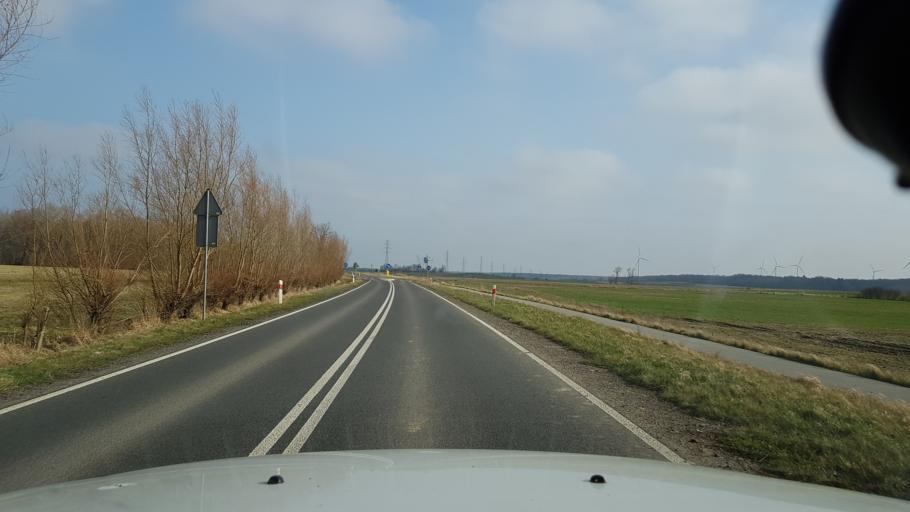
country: PL
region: West Pomeranian Voivodeship
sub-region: Powiat koszalinski
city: Sianow
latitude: 54.2972
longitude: 16.3062
